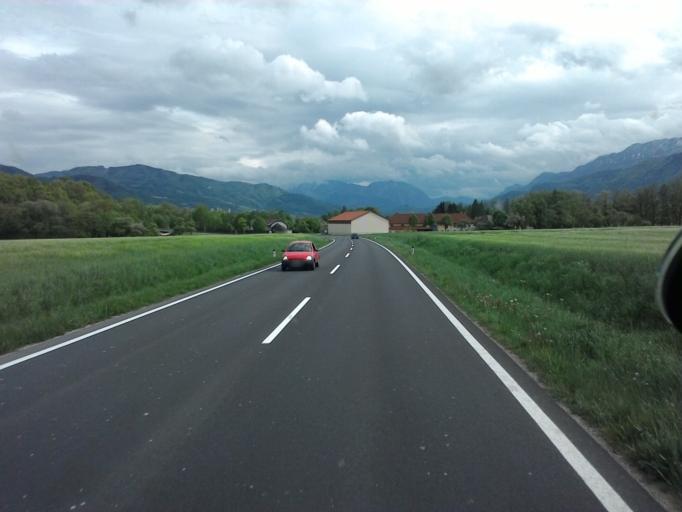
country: AT
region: Upper Austria
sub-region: Politischer Bezirk Kirchdorf an der Krems
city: Micheldorf in Oberoesterreich
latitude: 47.9261
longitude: 14.0893
